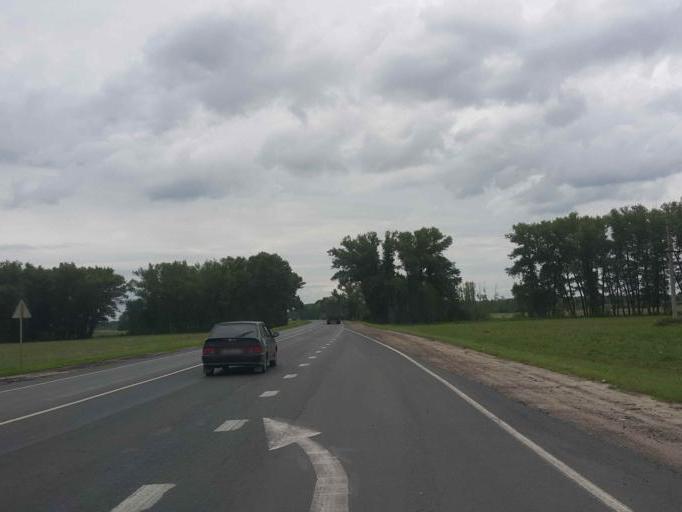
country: RU
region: Tambov
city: Zavoronezhskoye
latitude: 52.9526
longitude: 40.5813
